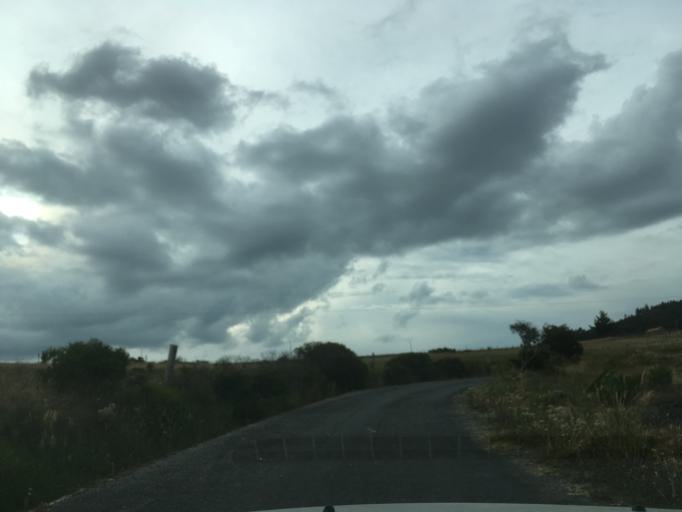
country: CO
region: Boyaca
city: Firavitoba
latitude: 5.6773
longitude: -73.0205
